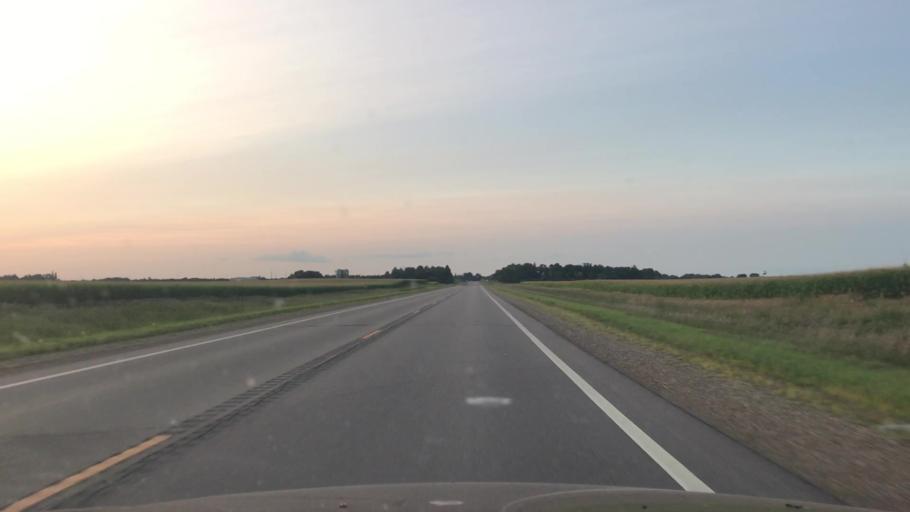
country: US
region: Minnesota
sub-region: Redwood County
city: Redwood Falls
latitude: 44.5102
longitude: -95.1180
